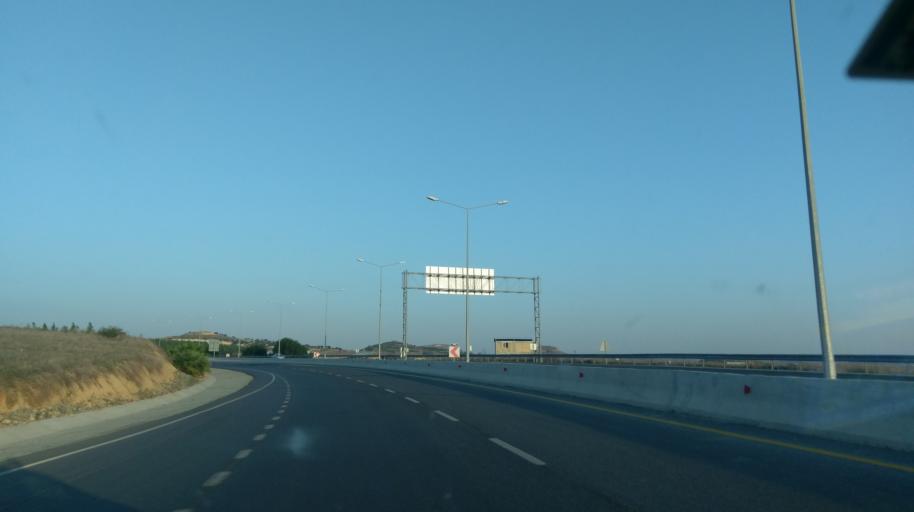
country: CY
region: Lefkosia
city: Akaki
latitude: 35.1951
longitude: 33.1103
